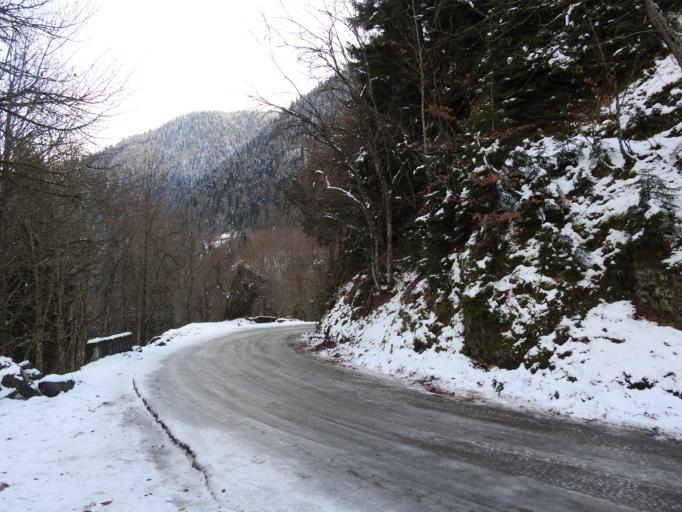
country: GE
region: Abkhazia
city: Gagra
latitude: 43.4799
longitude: 40.5495
